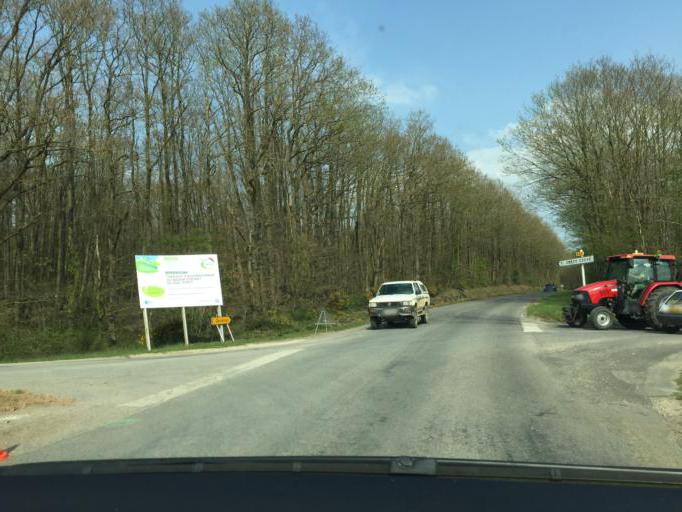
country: FR
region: Centre
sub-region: Departement d'Eure-et-Loir
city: Treon
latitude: 48.6667
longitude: 1.2646
